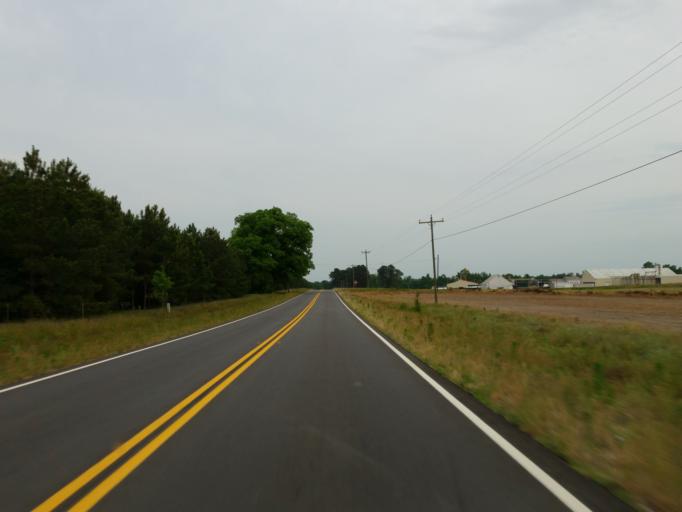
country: US
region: Georgia
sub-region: Dooly County
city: Unadilla
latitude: 32.2851
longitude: -83.7477
